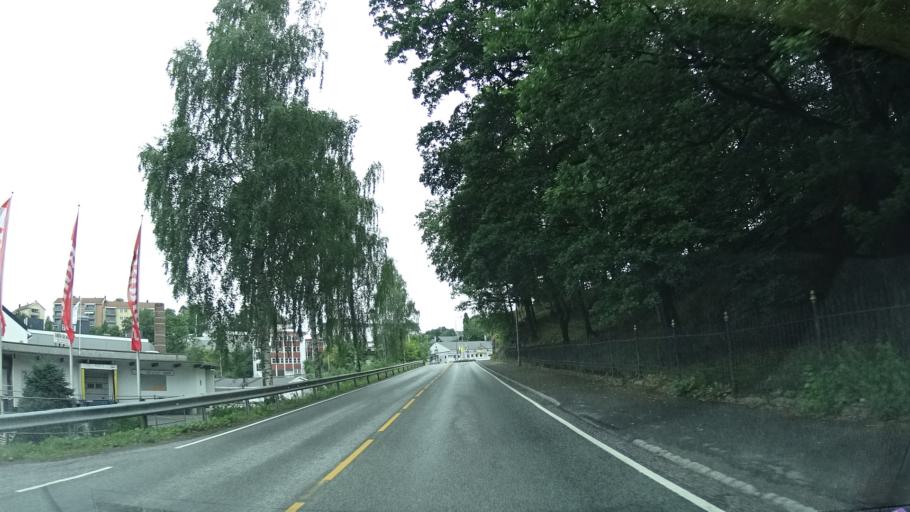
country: NO
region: Aust-Agder
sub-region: Arendal
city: Arendal
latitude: 58.4574
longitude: 8.7520
